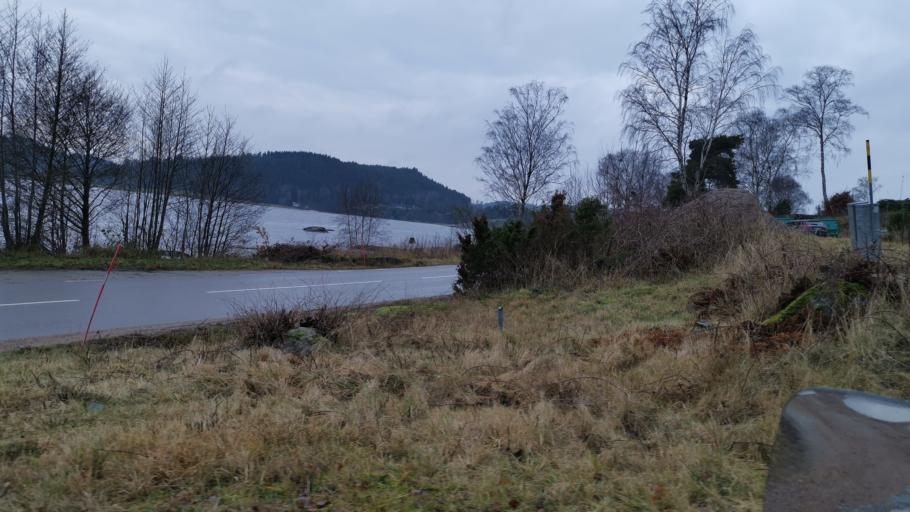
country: SE
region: Vaestra Goetaland
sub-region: Orust
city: Henan
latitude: 58.3382
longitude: 11.7149
